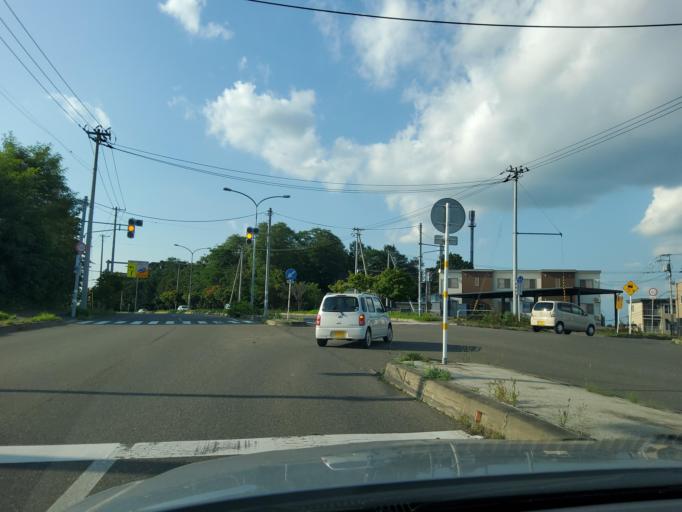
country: JP
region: Hokkaido
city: Obihiro
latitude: 42.9004
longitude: 143.1739
